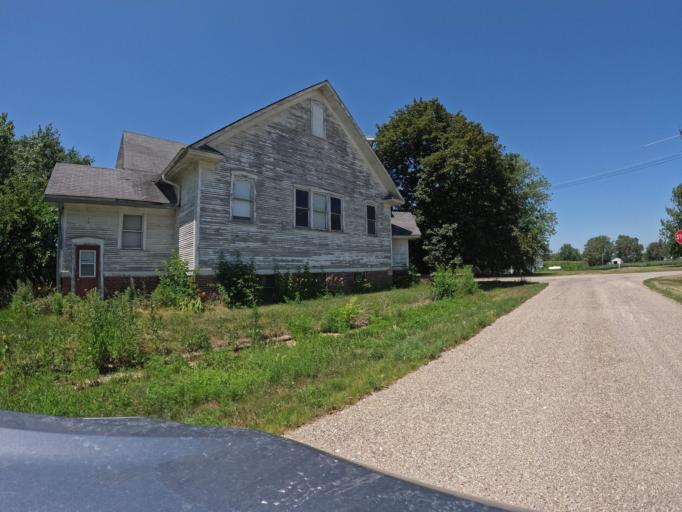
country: US
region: Iowa
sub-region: Keokuk County
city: Sigourney
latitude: 41.4550
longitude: -92.3348
